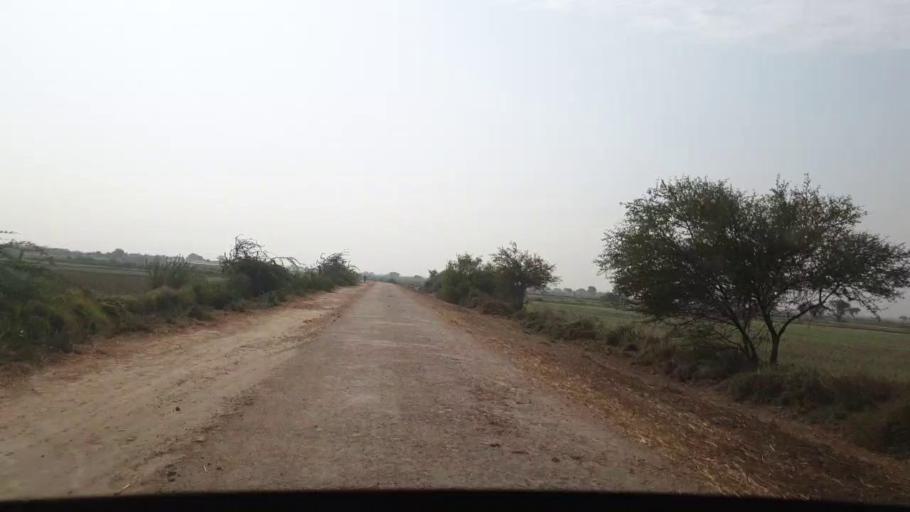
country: PK
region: Sindh
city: Chuhar Jamali
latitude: 24.3828
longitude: 67.9389
